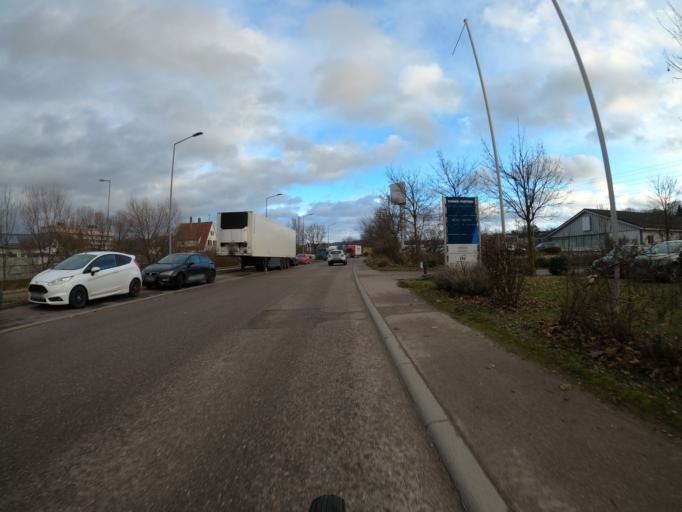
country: DE
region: Baden-Wuerttemberg
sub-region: Regierungsbezirk Stuttgart
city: Salach
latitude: 48.6848
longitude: 9.7323
